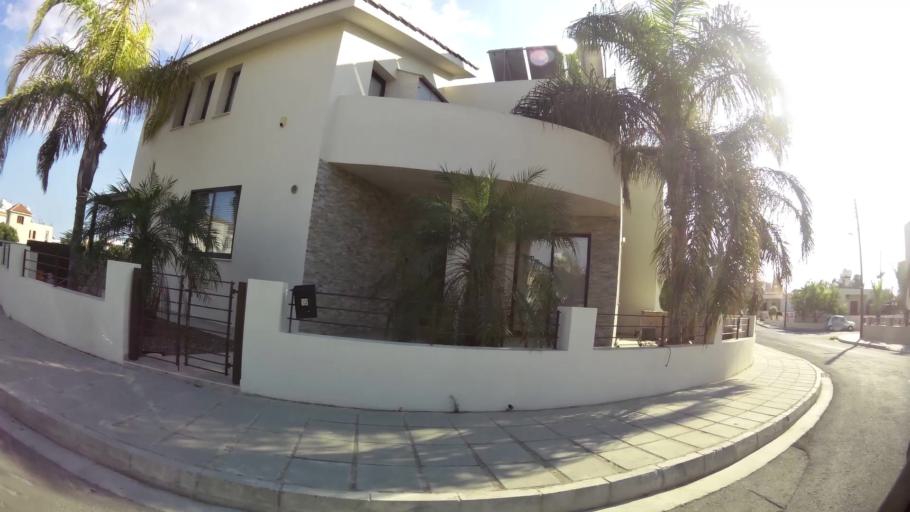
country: CY
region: Larnaka
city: Aradippou
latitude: 34.9491
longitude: 33.5967
